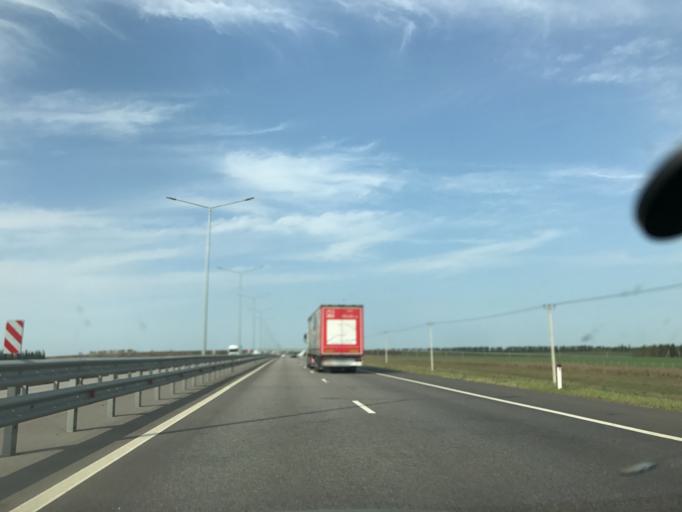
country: RU
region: Voronezj
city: Podkletnoye
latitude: 51.4989
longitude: 39.5235
